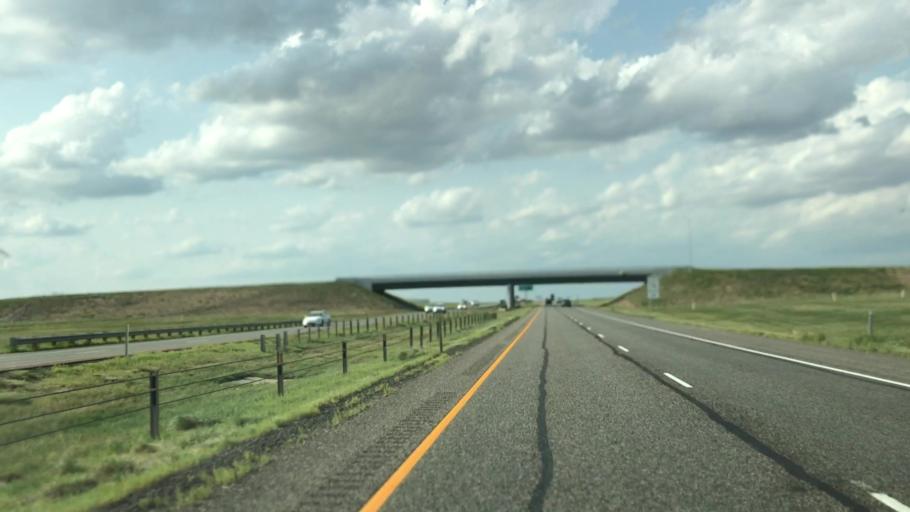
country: US
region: Colorado
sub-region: Adams County
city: Aurora
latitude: 39.7817
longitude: -104.7163
